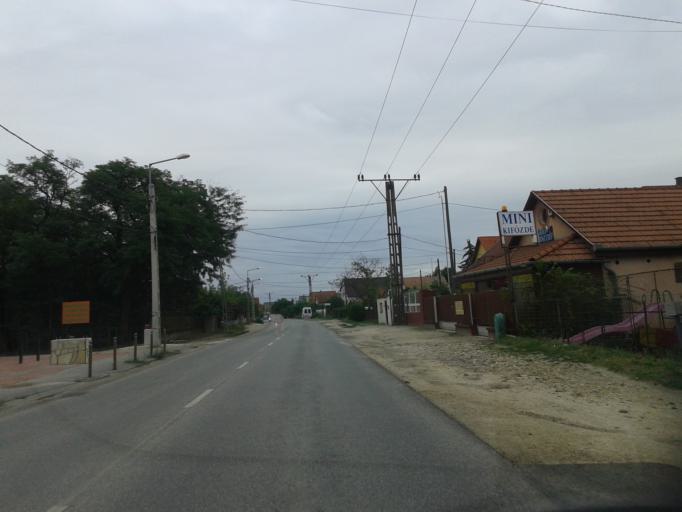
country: HU
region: Pest
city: Szigethalom
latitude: 47.3255
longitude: 19.0096
